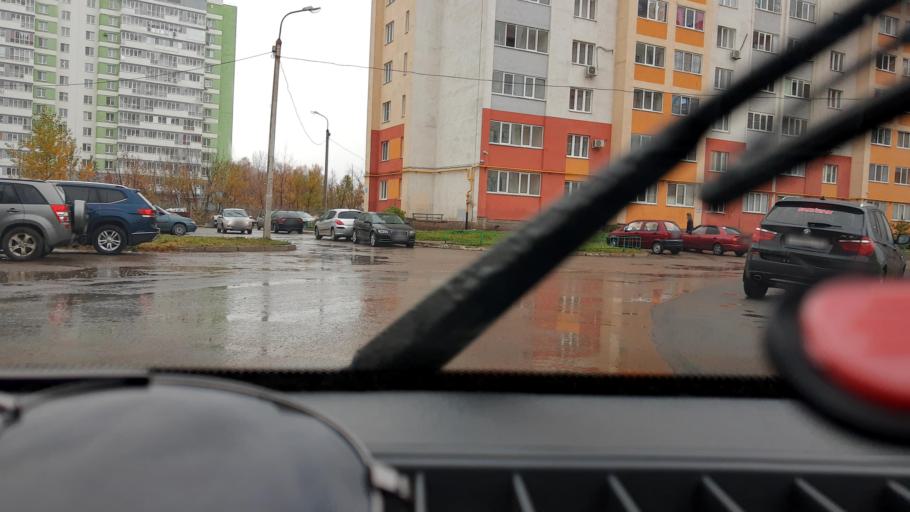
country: RU
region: Bashkortostan
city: Ufa
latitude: 54.7845
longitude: 56.1128
